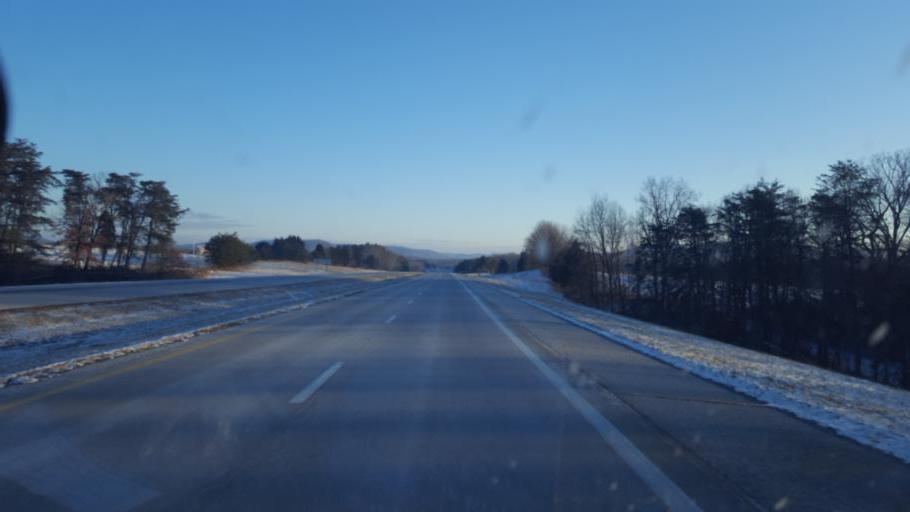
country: US
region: Ohio
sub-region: Adams County
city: Peebles
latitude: 38.9636
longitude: -83.3541
